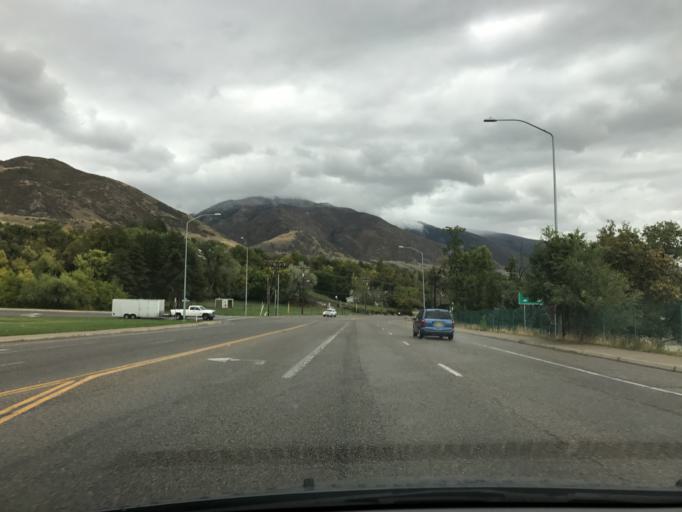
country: US
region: Utah
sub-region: Davis County
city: Fruit Heights
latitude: 41.0107
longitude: -111.9107
